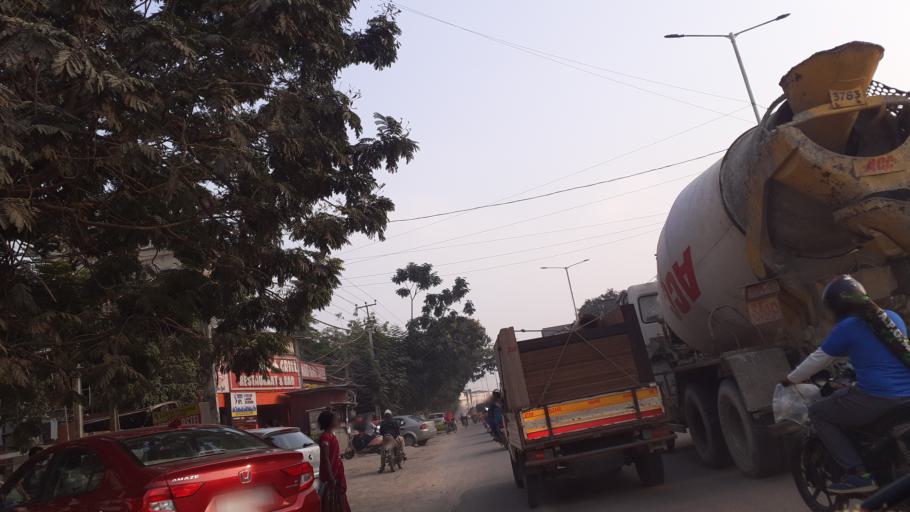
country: IN
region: Telangana
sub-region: Rangareddi
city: Kukatpalli
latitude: 17.4700
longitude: 78.3656
